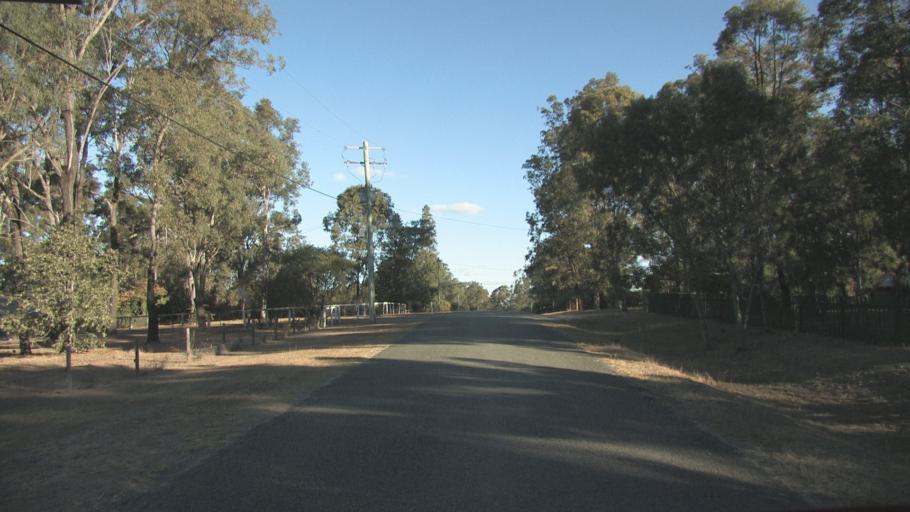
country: AU
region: Queensland
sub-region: Logan
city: Cedar Vale
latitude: -27.8641
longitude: 152.9744
